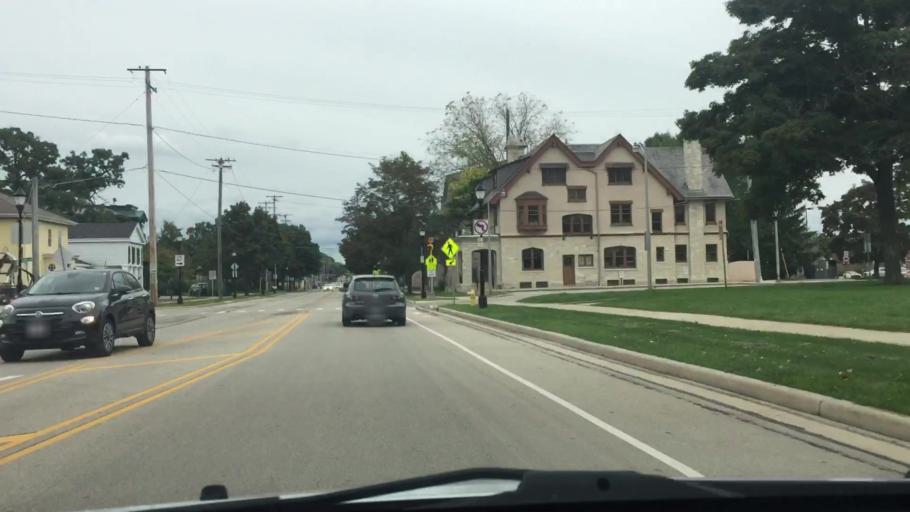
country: US
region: Wisconsin
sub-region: Waukesha County
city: Waukesha
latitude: 43.0093
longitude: -88.2316
